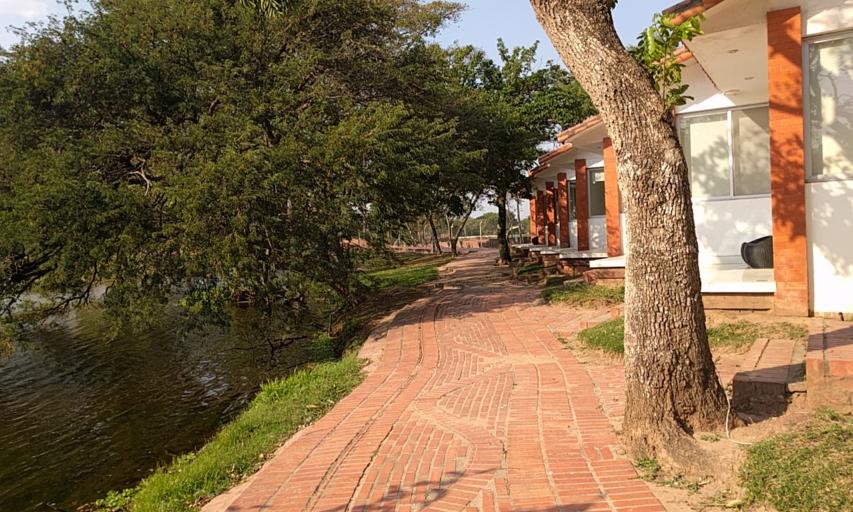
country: BO
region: Santa Cruz
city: Warnes
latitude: -17.4465
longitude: -63.1842
